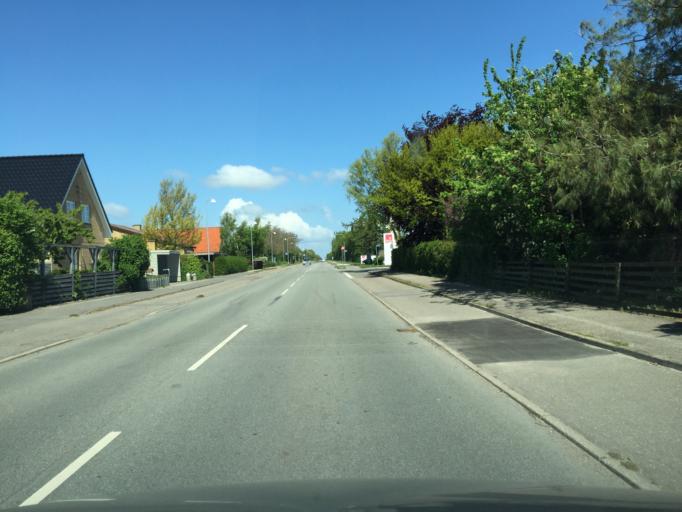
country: DK
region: Zealand
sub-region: Vordingborg Kommune
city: Stege
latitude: 54.9932
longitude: 12.2841
